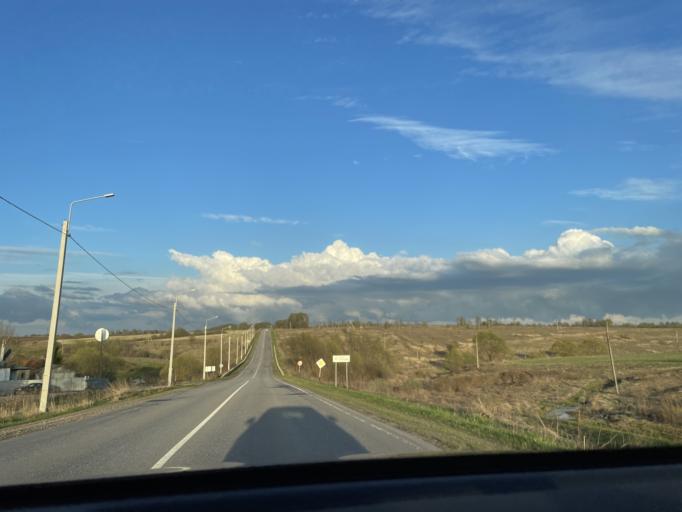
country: RU
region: Tula
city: Novogurovskiy
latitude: 54.5246
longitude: 37.4207
